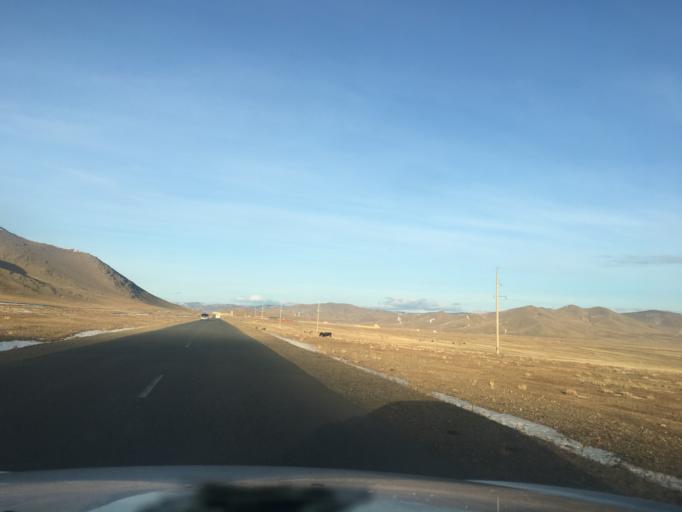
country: MN
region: Central Aimak
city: Mandal
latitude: 48.1134
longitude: 106.6400
